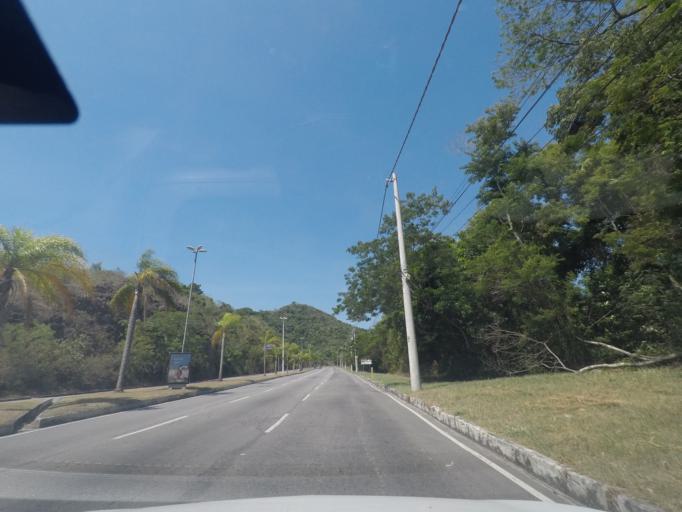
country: BR
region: Rio de Janeiro
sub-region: Niteroi
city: Niteroi
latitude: -22.9269
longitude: -43.0623
